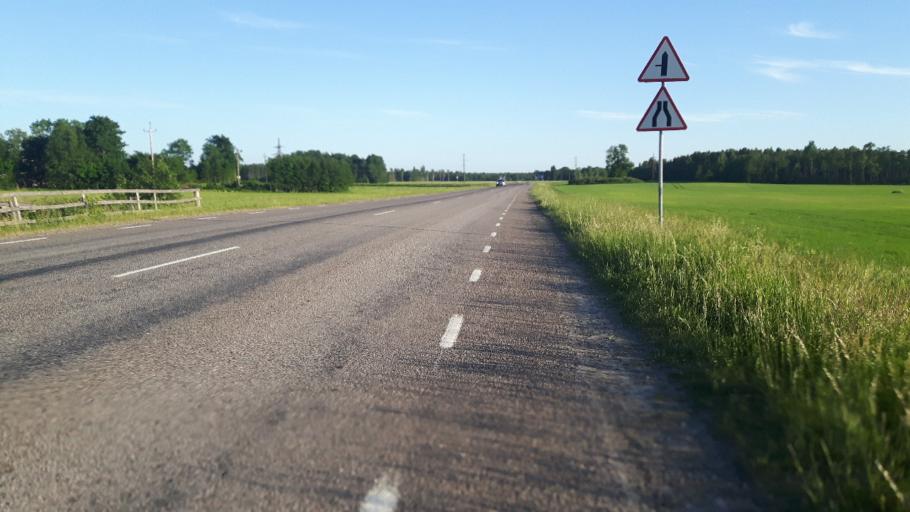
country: EE
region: Raplamaa
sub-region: Jaervakandi vald
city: Jarvakandi
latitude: 58.7926
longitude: 24.9278
